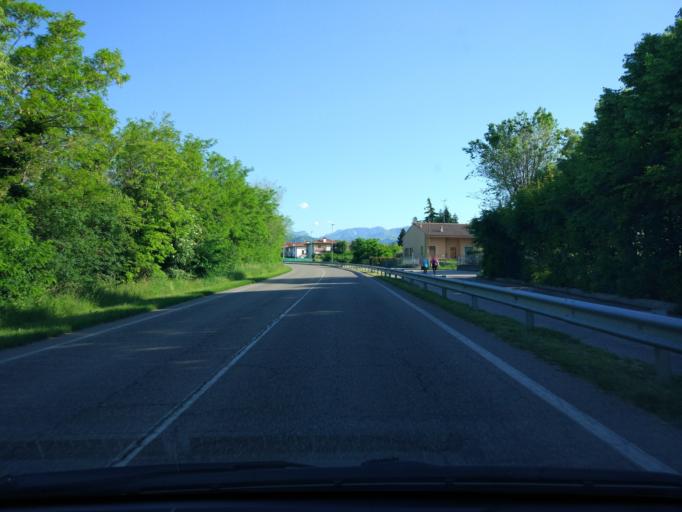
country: IT
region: Veneto
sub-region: Provincia di Verona
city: Tregnago
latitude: 45.5159
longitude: 11.1608
